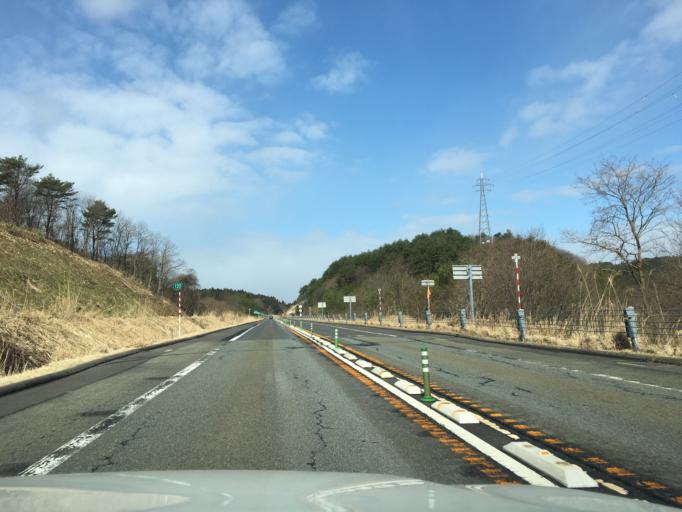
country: JP
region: Akita
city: Akita
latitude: 39.7599
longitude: 140.1315
